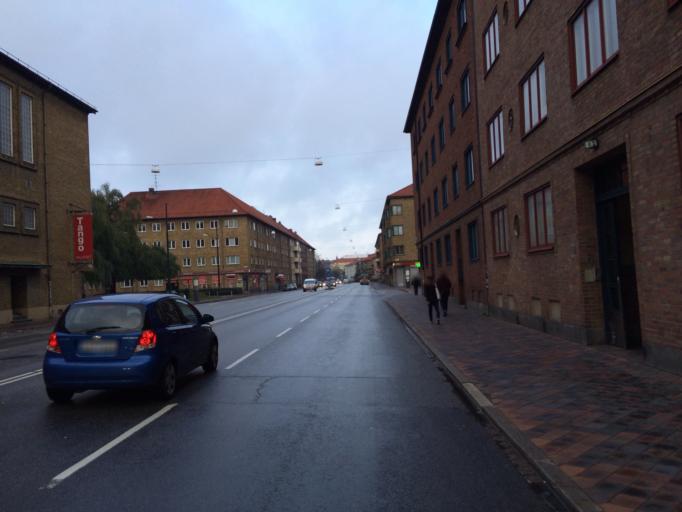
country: SE
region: Skane
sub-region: Malmo
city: Malmoe
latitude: 55.5930
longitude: 13.0189
